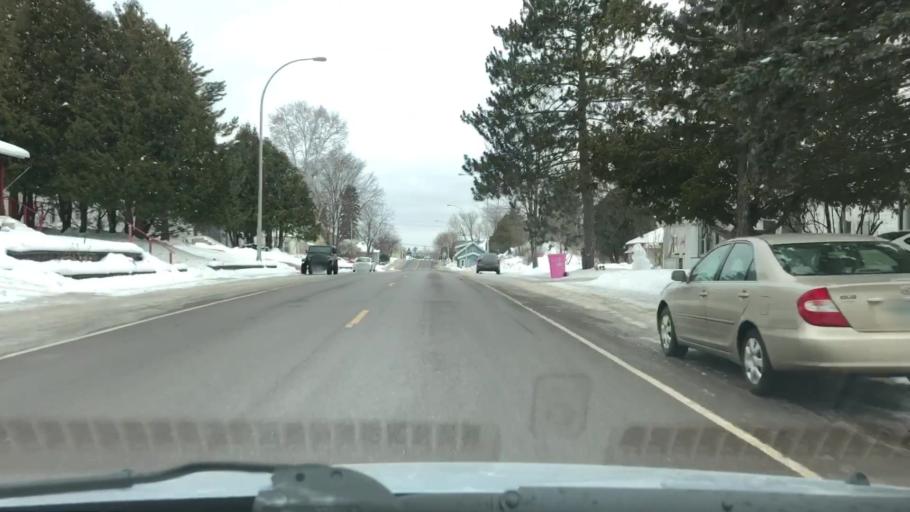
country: US
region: Minnesota
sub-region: Carlton County
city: Carlton
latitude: 46.6640
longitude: -92.4205
